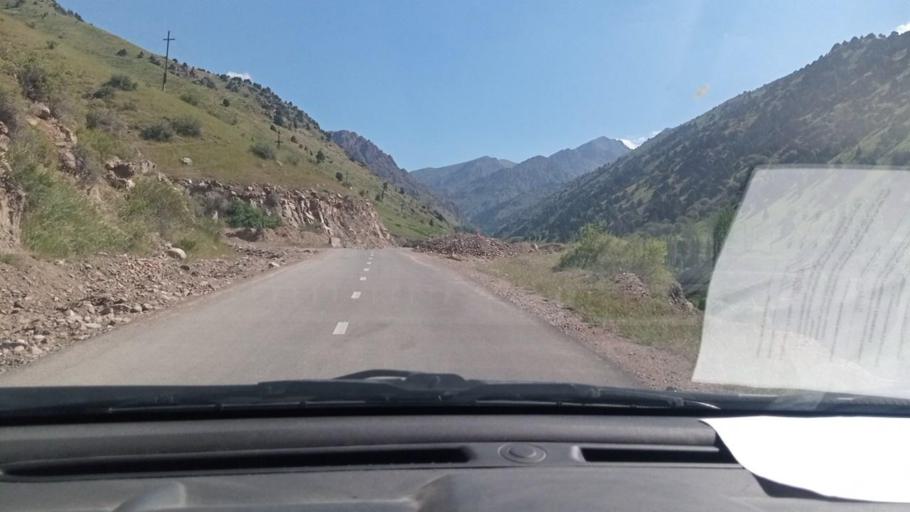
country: UZ
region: Toshkent
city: Yangiobod
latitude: 41.1269
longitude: 70.1084
